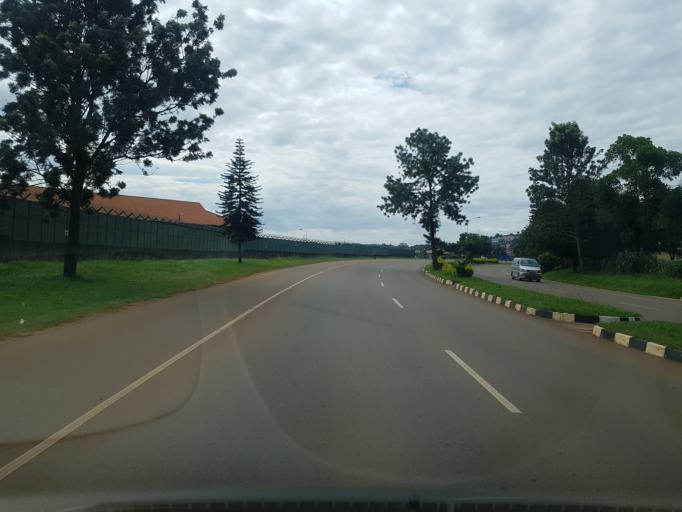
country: UG
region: Central Region
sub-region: Wakiso District
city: Entebbe
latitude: 0.0508
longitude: 32.4568
